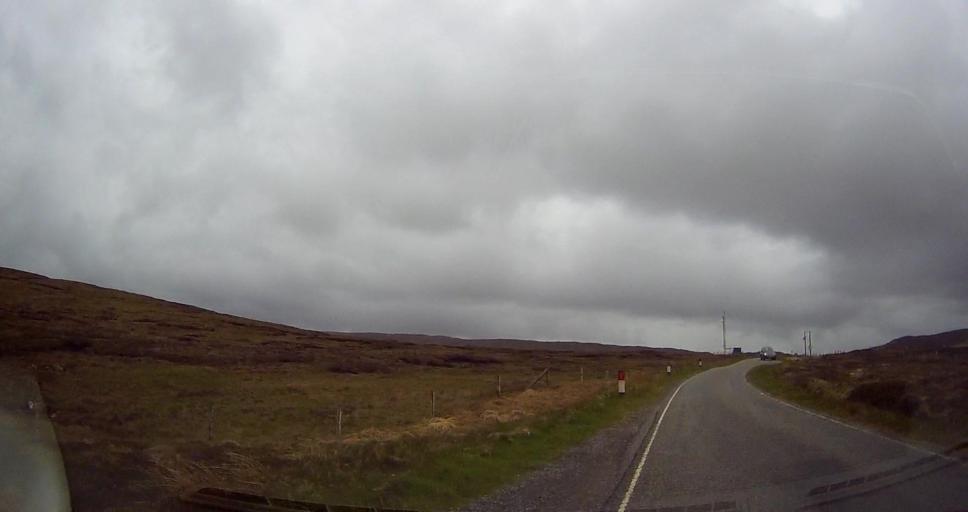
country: GB
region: Scotland
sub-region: Shetland Islands
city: Lerwick
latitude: 60.2766
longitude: -1.2602
